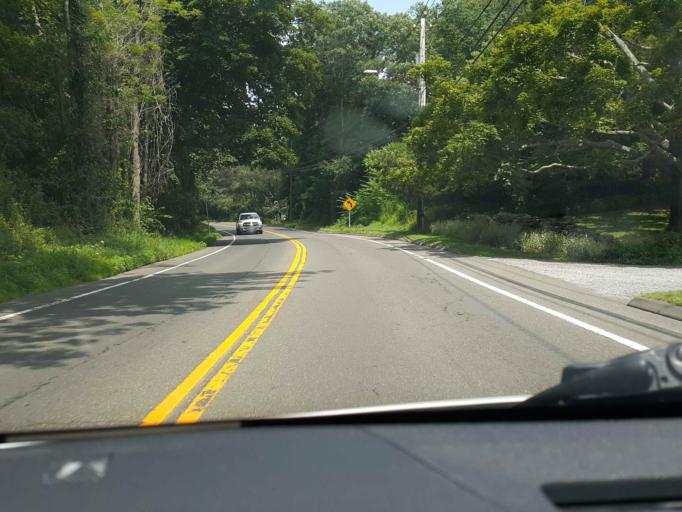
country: US
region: Connecticut
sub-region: New Haven County
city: Guilford
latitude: 41.3007
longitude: -72.6871
